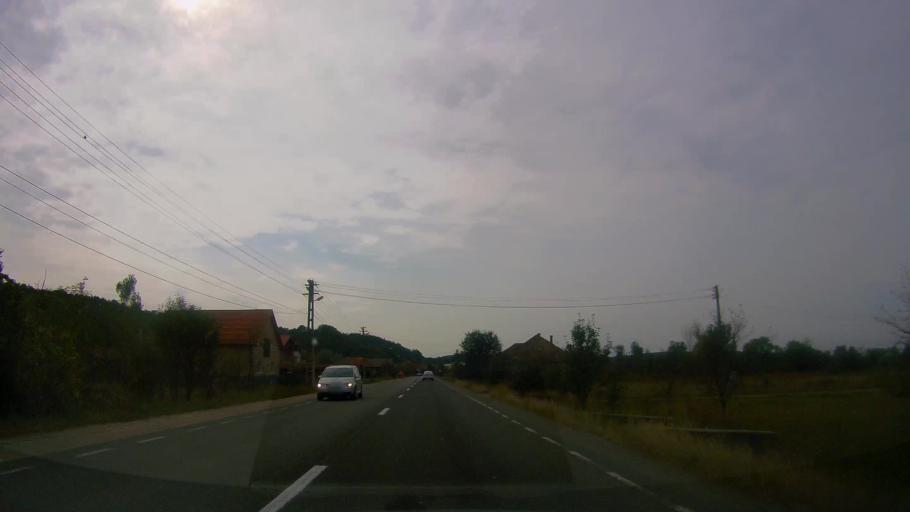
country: RO
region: Salaj
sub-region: Comuna Romanasi
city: Romanasi
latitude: 47.0932
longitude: 23.1891
